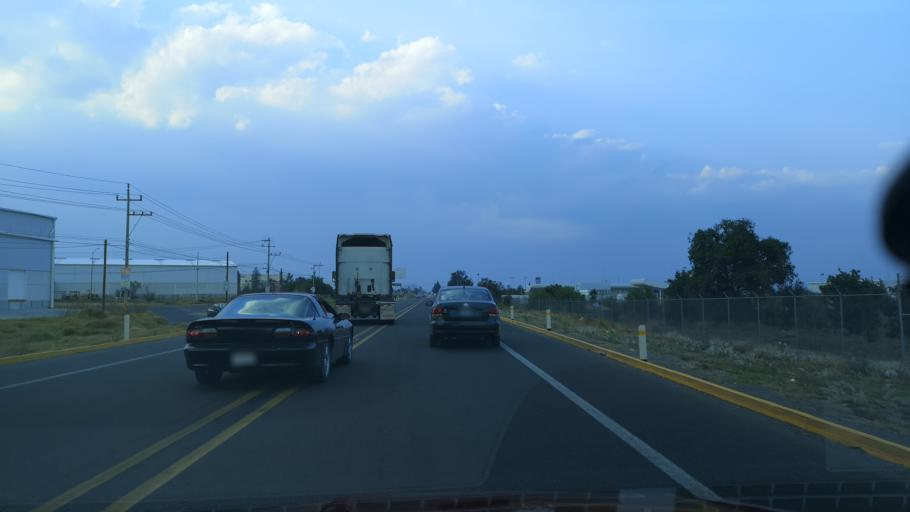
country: MX
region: Puebla
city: Huejotzingo
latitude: 19.1551
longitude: -98.3771
